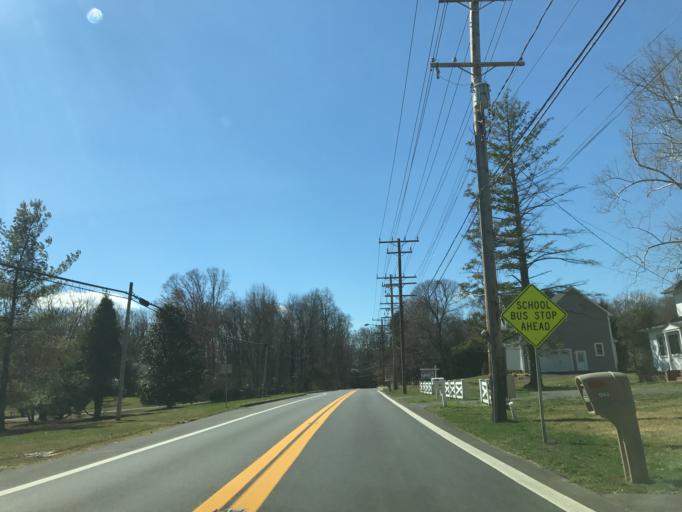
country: US
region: Maryland
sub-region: Anne Arundel County
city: Naval Academy
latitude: 39.0040
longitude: -76.4761
